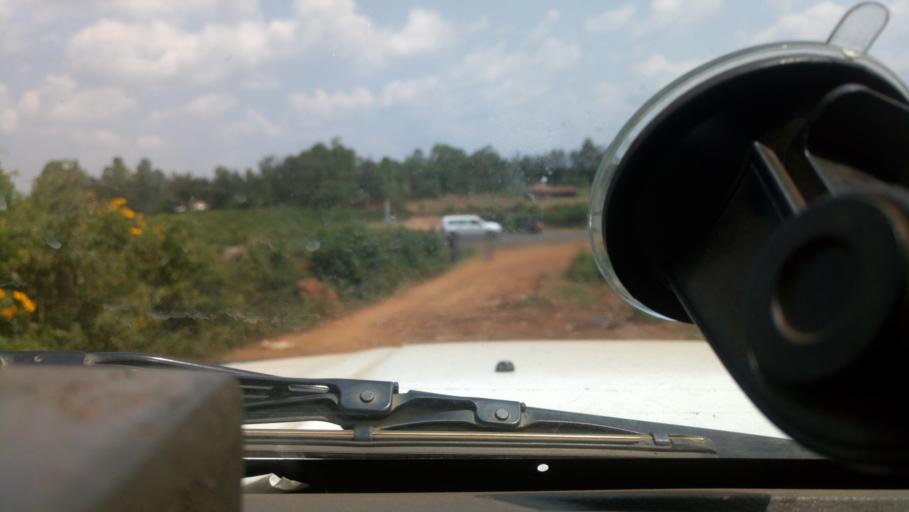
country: KE
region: Kisii
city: Ogembo
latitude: -0.7769
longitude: 34.5989
